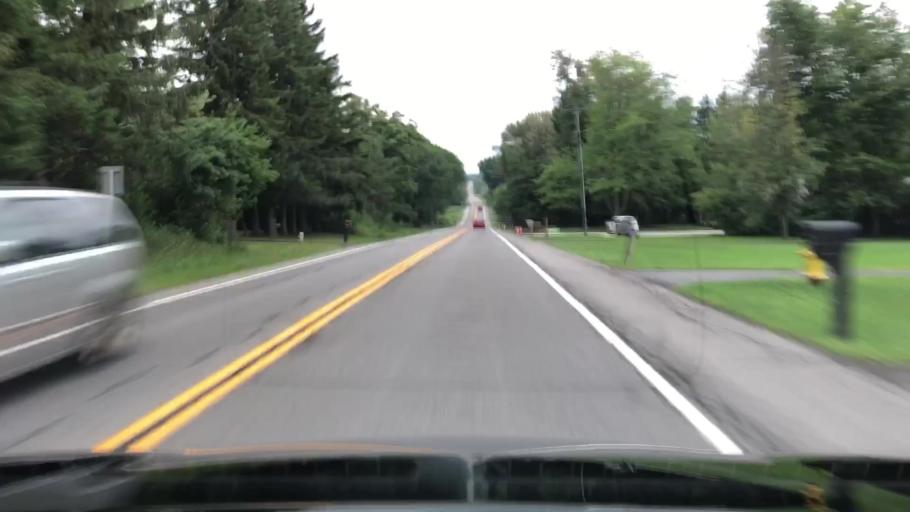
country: US
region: New York
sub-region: Erie County
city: Orchard Park
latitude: 42.7848
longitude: -78.6969
